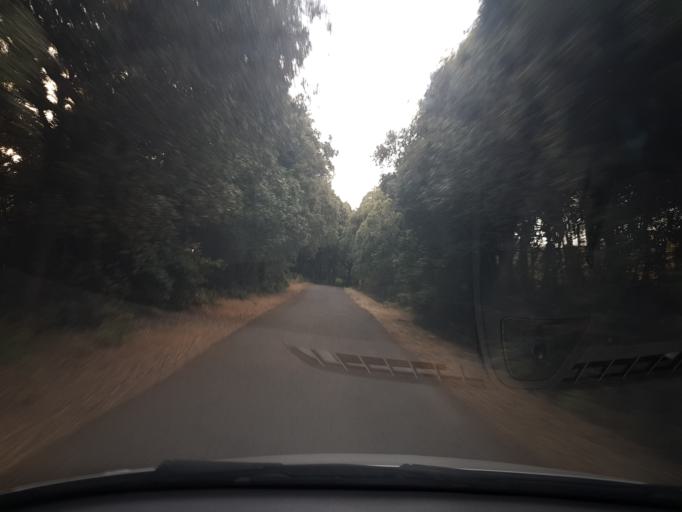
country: IT
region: Sardinia
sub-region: Provincia di Oristano
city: Seneghe
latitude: 40.1104
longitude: 8.5855
